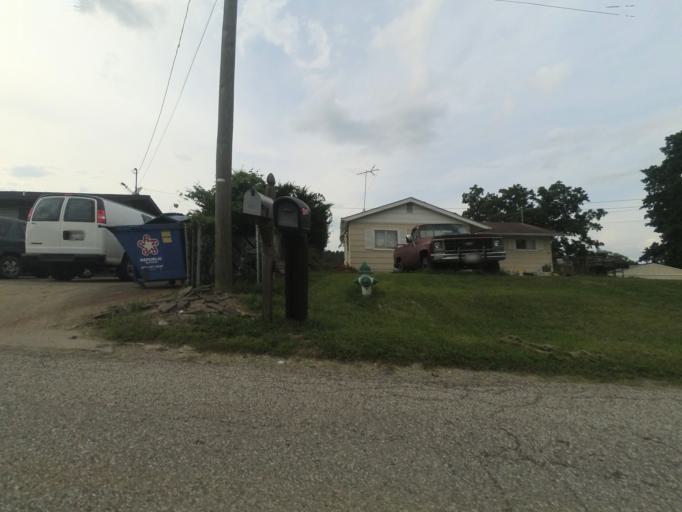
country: US
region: West Virginia
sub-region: Cabell County
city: Huntington
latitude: 38.3850
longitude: -82.4148
